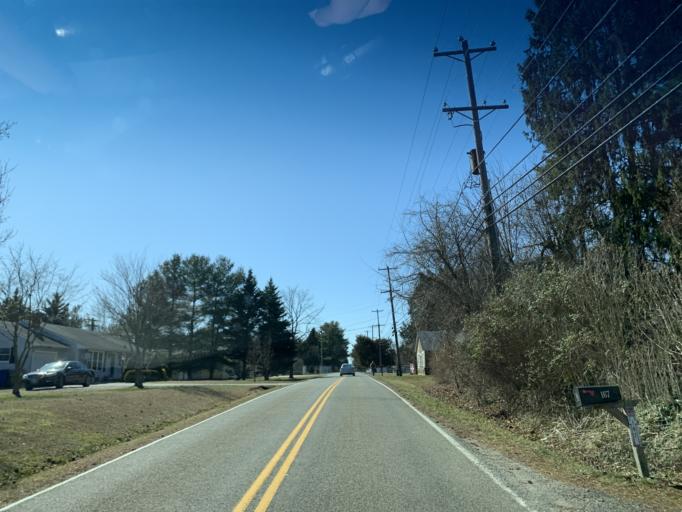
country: US
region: Maryland
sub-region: Cecil County
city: Elkton
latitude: 39.5203
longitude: -75.8208
